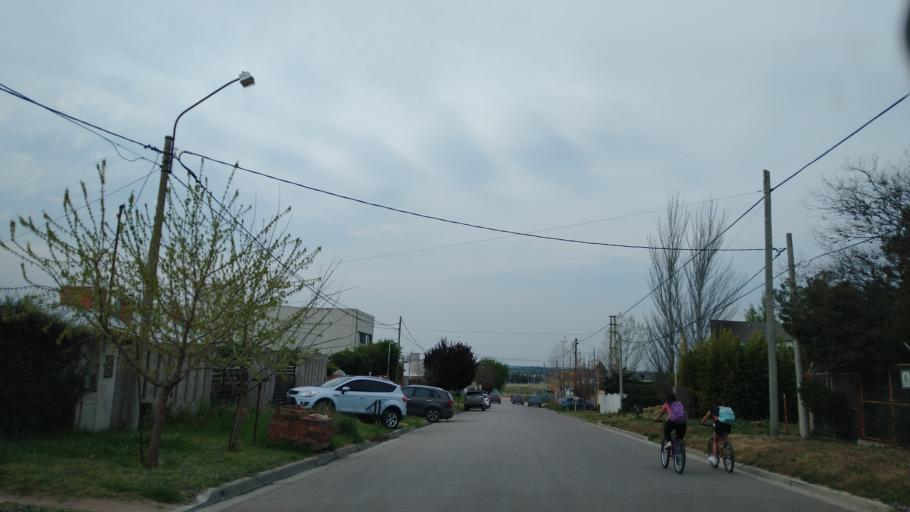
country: AR
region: Buenos Aires
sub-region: Partido de Bahia Blanca
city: Bahia Blanca
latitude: -38.6981
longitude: -62.2366
